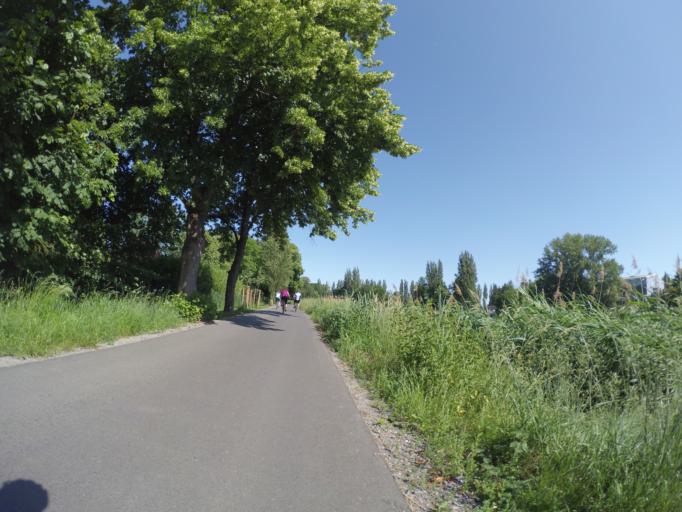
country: CZ
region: Central Bohemia
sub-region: Okres Nymburk
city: Nymburk
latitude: 50.1799
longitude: 15.0605
